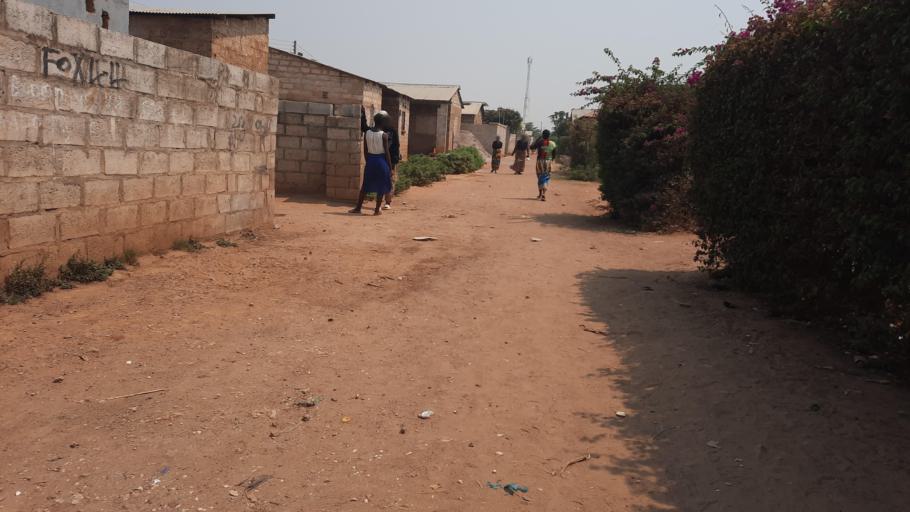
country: ZM
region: Lusaka
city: Lusaka
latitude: -15.3989
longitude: 28.3793
